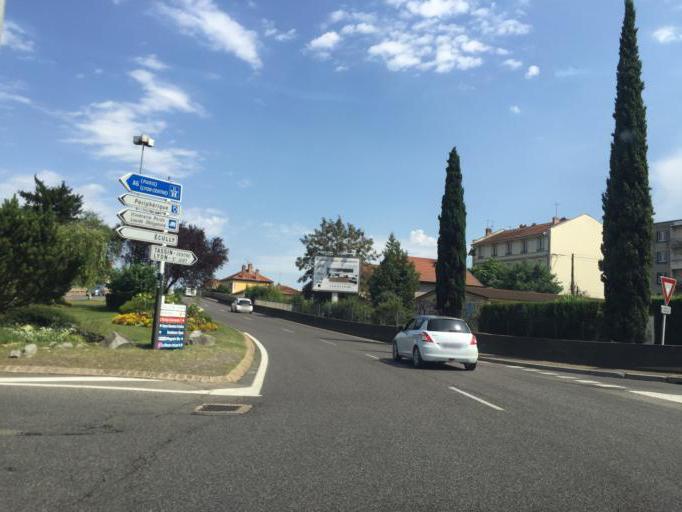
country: FR
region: Rhone-Alpes
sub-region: Departement du Rhone
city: Ecully
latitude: 45.7641
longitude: 4.7692
